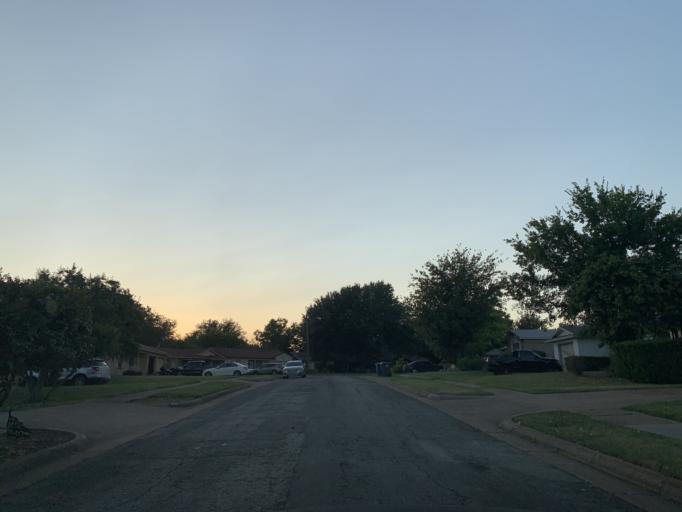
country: US
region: Texas
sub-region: Dallas County
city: Lancaster
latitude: 32.6704
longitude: -96.8015
